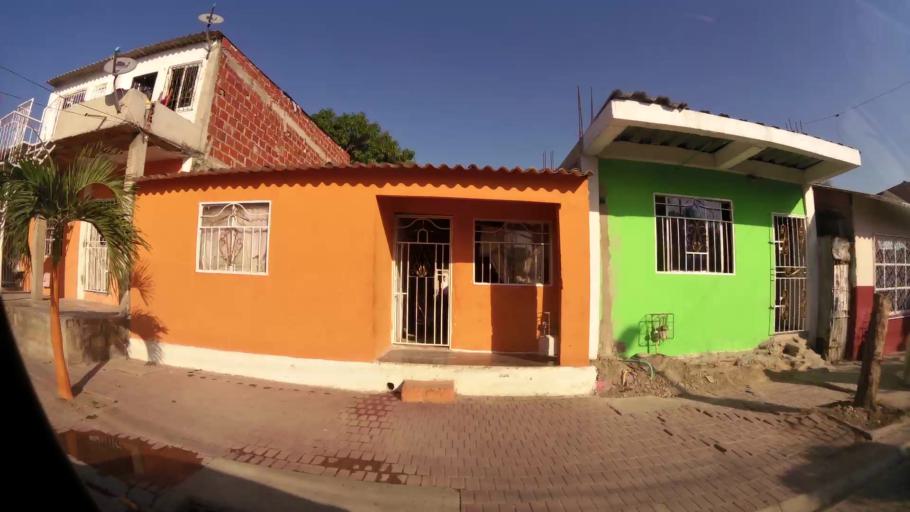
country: CO
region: Bolivar
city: Cartagena
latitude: 10.4118
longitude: -75.4961
